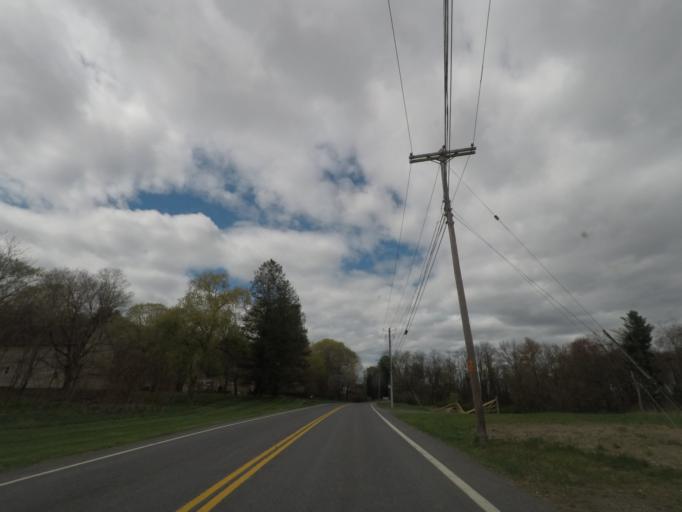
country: US
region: New York
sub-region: Columbia County
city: Philmont
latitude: 42.2620
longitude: -73.6662
